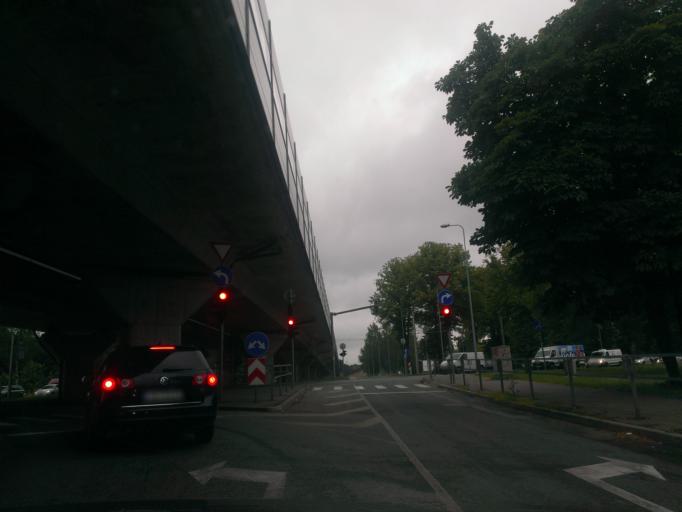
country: LV
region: Riga
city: Jaunciems
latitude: 56.9858
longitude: 24.1605
